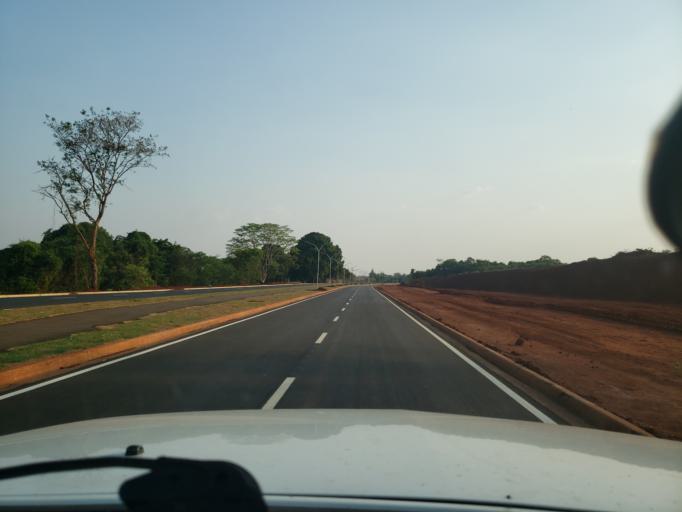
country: BR
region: Sao Paulo
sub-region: Moji-Guacu
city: Mogi-Gaucu
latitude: -22.3207
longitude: -46.9472
